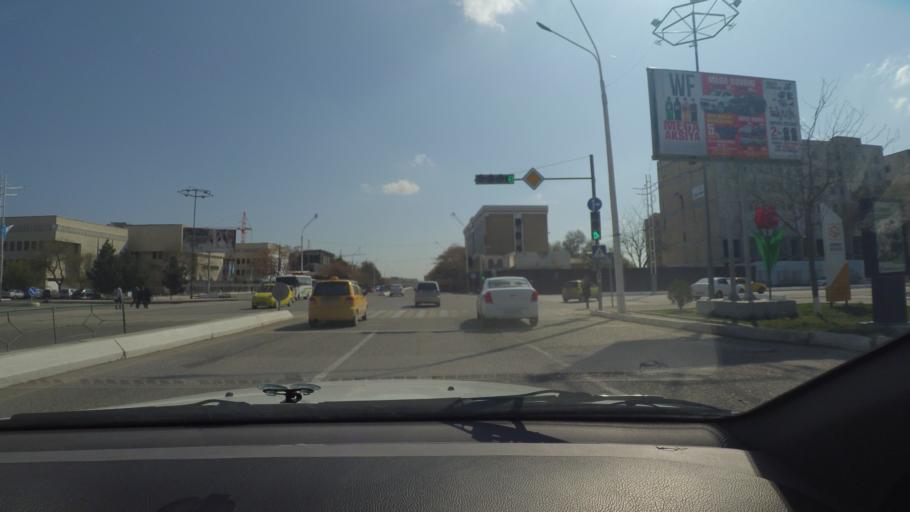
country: UZ
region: Bukhara
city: Bukhara
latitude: 39.7706
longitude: 64.4306
